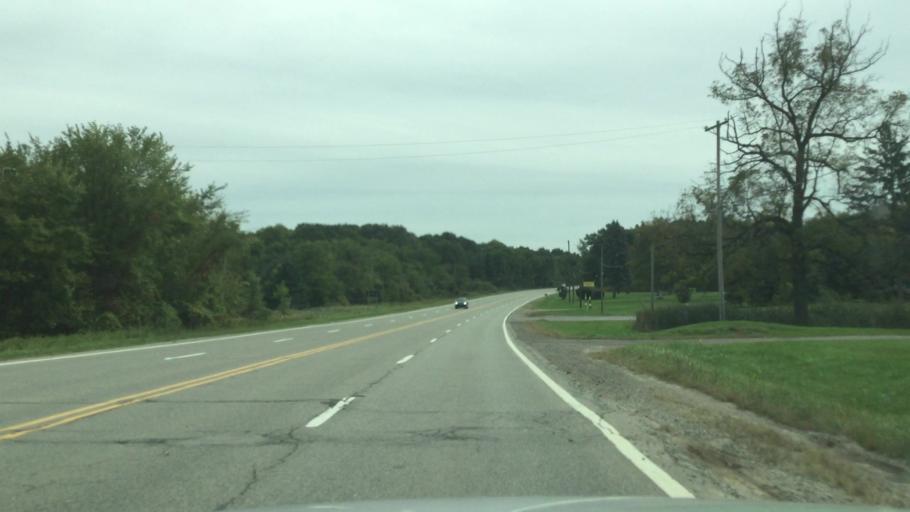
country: US
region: Michigan
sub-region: Oakland County
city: Ortonville
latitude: 42.8003
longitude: -83.5279
